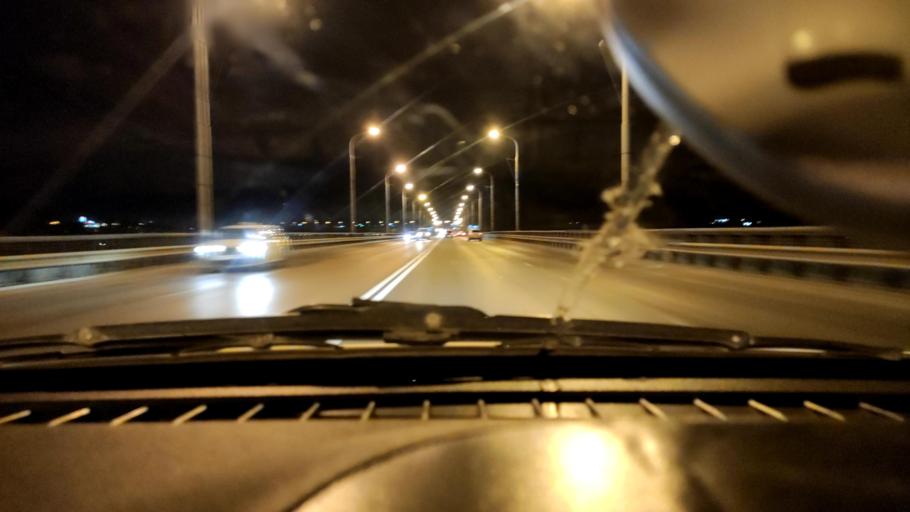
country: RU
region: Perm
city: Perm
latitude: 58.0202
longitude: 56.2206
